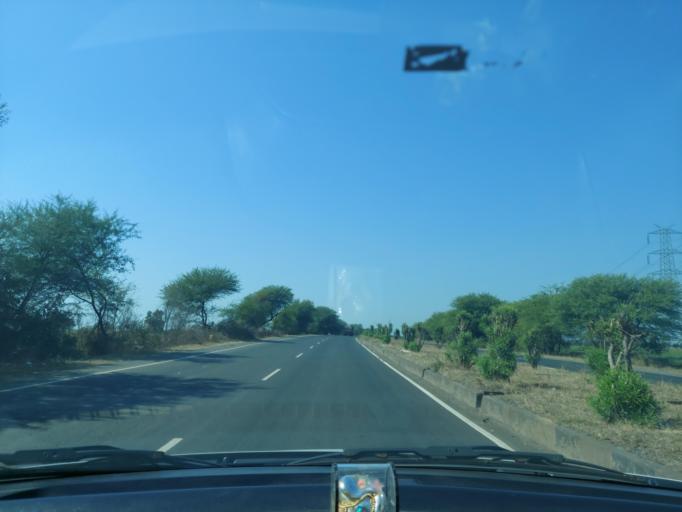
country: IN
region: Madhya Pradesh
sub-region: Indore
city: Manpur
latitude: 22.5024
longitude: 75.5544
